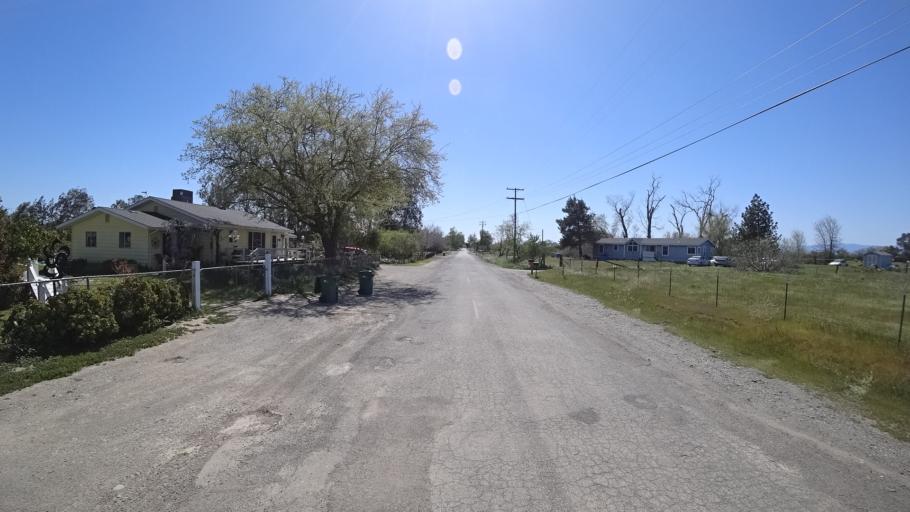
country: US
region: California
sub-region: Glenn County
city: Orland
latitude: 39.7789
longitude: -122.2477
